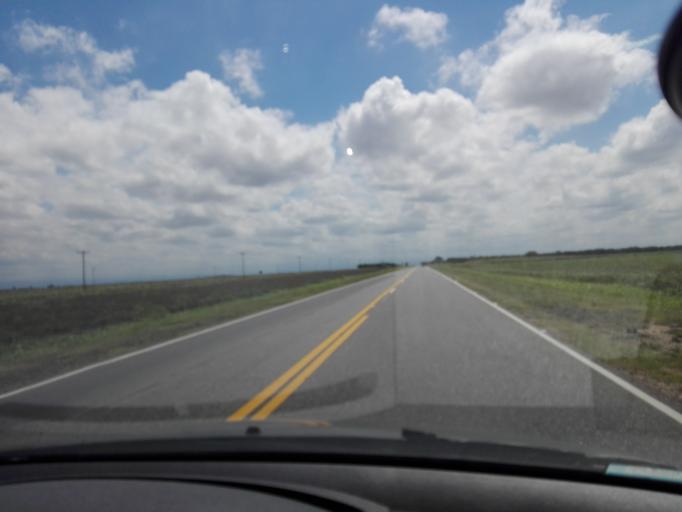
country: AR
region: Cordoba
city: Toledo
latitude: -31.6491
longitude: -64.1262
